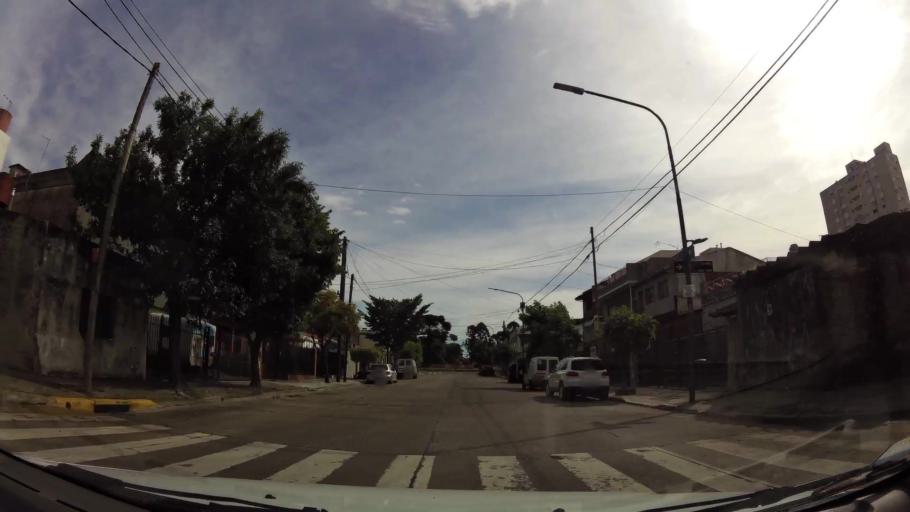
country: AR
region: Buenos Aires F.D.
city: Villa Lugano
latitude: -34.6663
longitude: -58.5105
